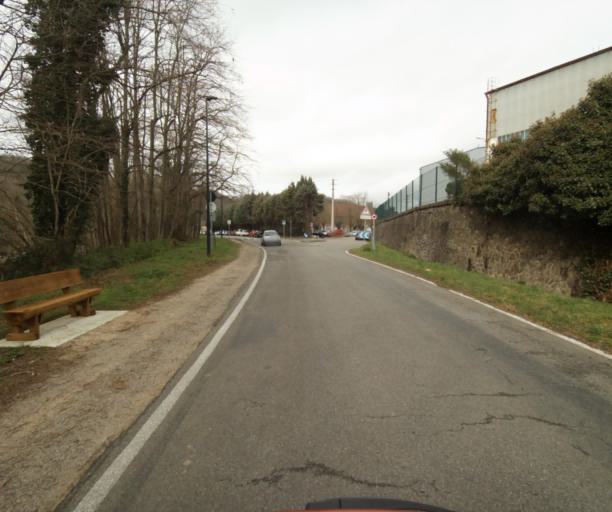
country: FR
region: Midi-Pyrenees
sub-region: Departement de l'Ariege
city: Pamiers
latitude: 43.1172
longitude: 1.6021
